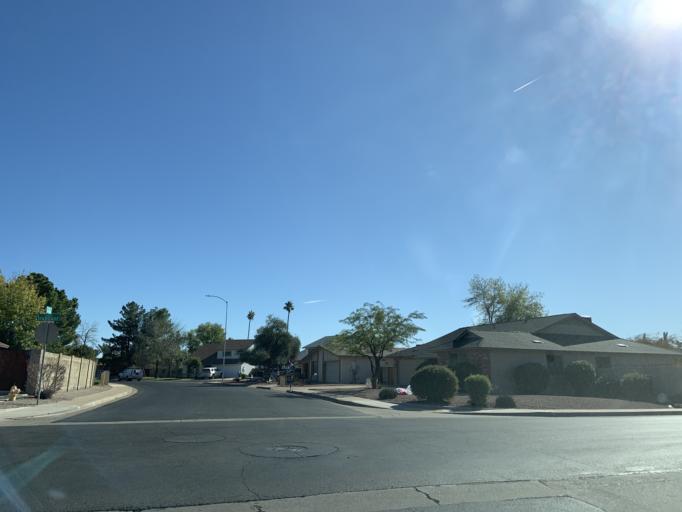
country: US
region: Arizona
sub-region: Maricopa County
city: San Carlos
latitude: 33.3741
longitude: -111.8648
